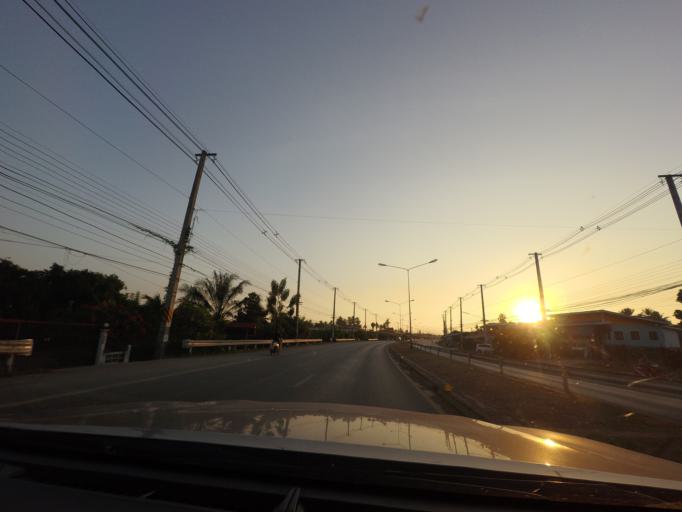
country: TH
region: Sukhothai
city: Sukhothai
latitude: 17.0618
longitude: 99.8393
